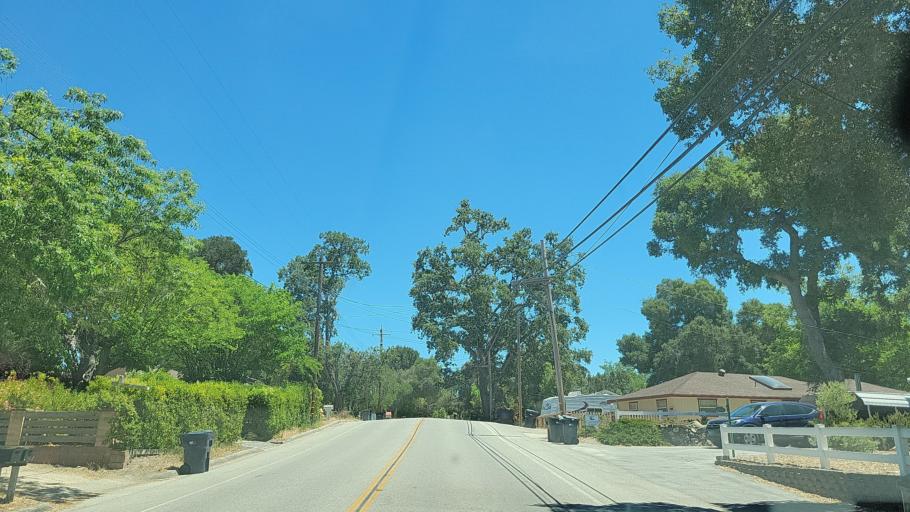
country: US
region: California
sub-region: San Luis Obispo County
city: Atascadero
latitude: 35.4691
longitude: -120.6606
